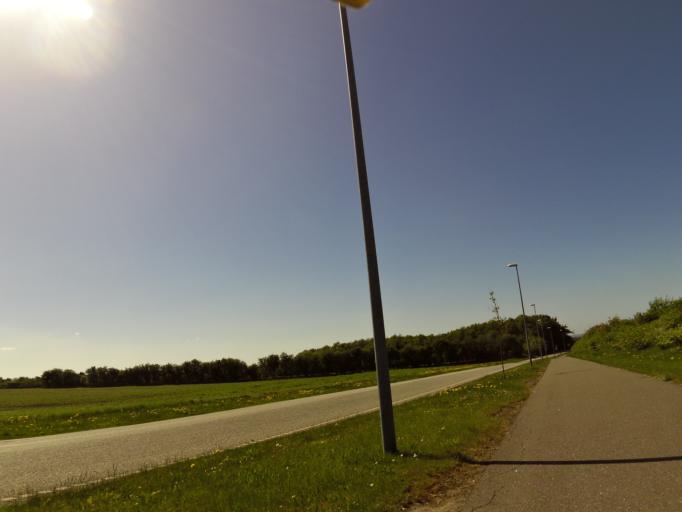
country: DK
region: Central Jutland
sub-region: Holstebro Kommune
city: Vinderup
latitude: 56.4693
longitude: 8.7934
